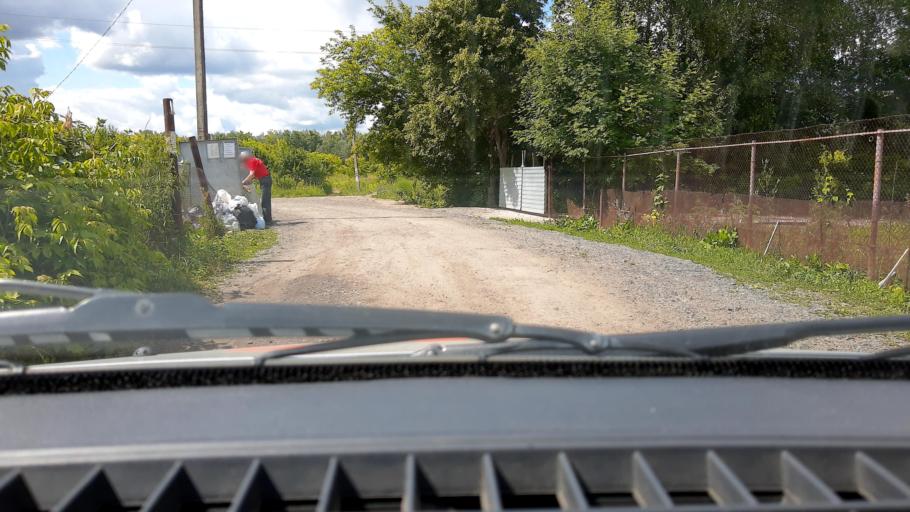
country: RU
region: Bashkortostan
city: Ufa
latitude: 54.6930
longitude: 56.0505
